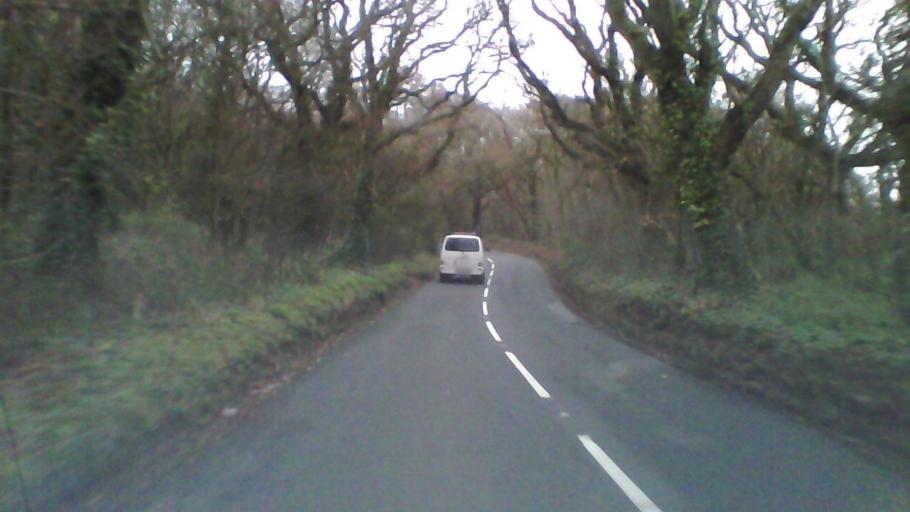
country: GB
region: England
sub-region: Isle of Wight
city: Bembridge
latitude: 50.6784
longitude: -1.0994
